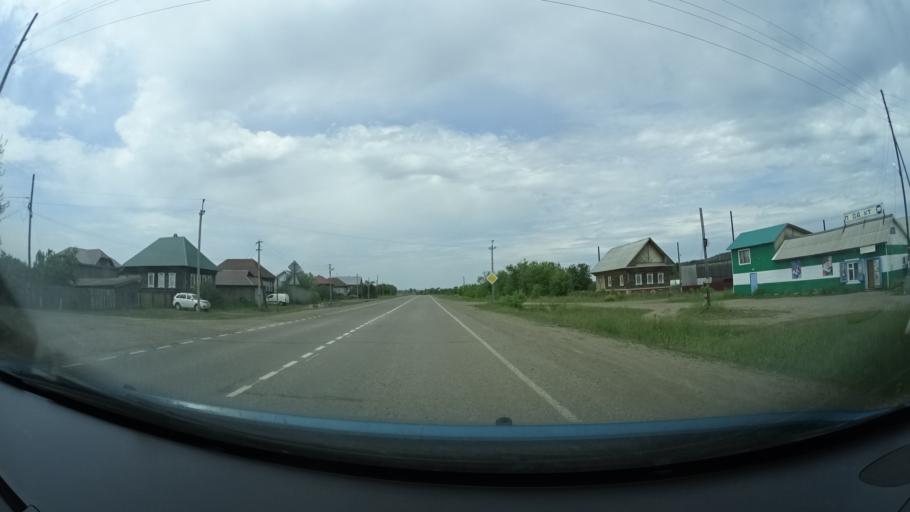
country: RU
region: Perm
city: Barda
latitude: 56.8279
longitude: 55.6263
